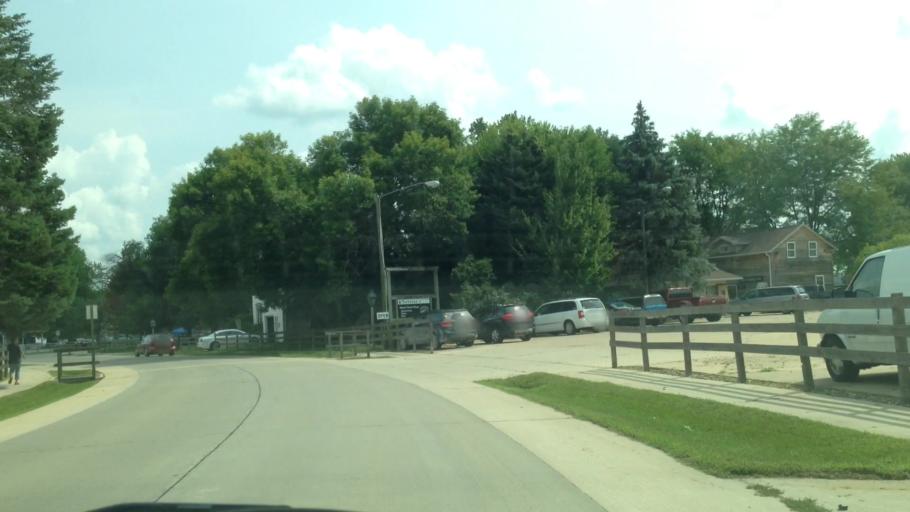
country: US
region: Iowa
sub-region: Benton County
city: Walford
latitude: 41.7988
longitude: -91.8662
